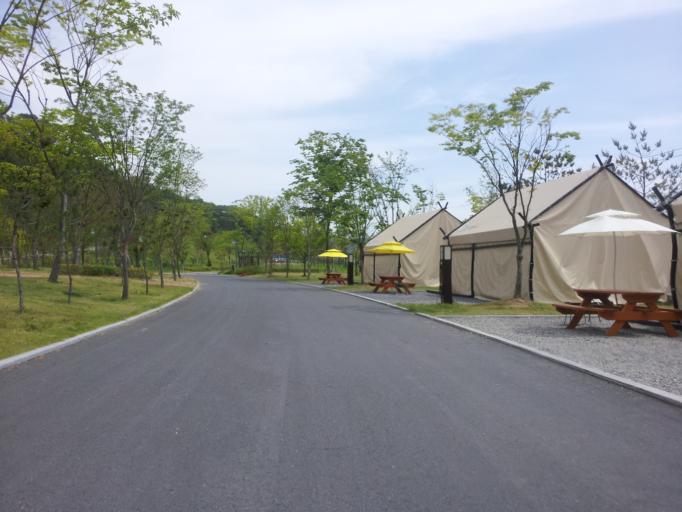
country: KR
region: Daejeon
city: Sintansin
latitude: 36.4550
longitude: 127.4754
